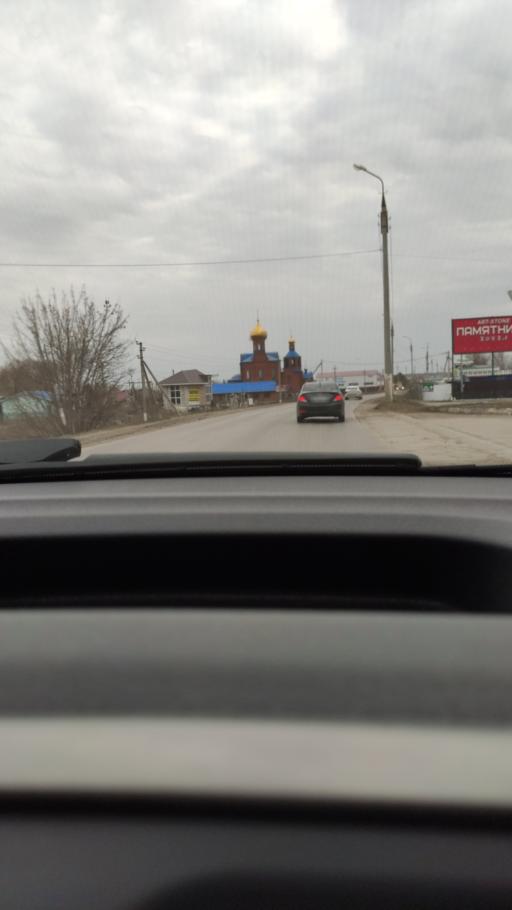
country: RU
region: Samara
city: Tol'yatti
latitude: 53.5750
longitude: 49.4016
